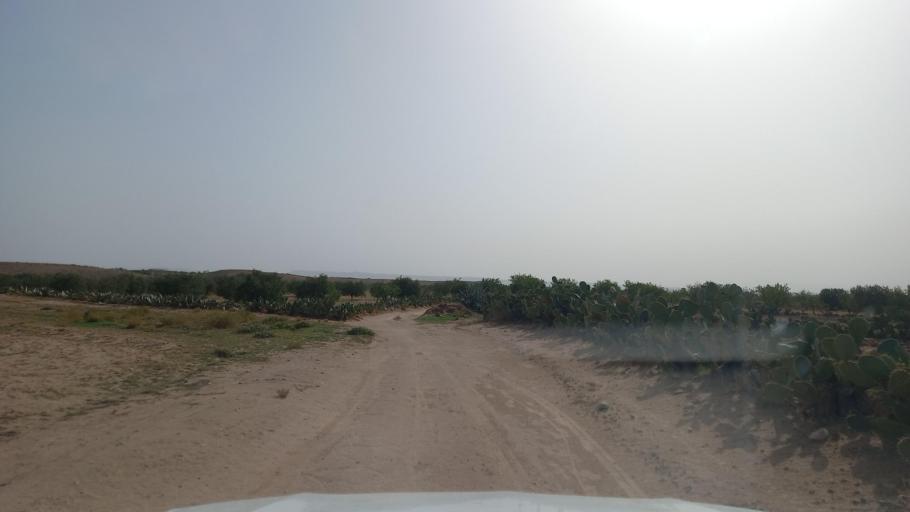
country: TN
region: Al Qasrayn
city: Kasserine
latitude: 35.2964
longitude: 8.9633
